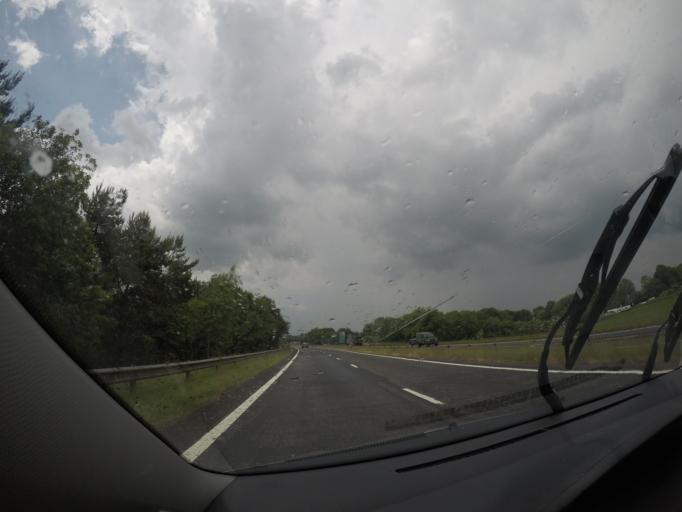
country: GB
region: England
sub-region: Cumbria
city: Appleby-in-Westmorland
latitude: 54.5866
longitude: -2.4942
